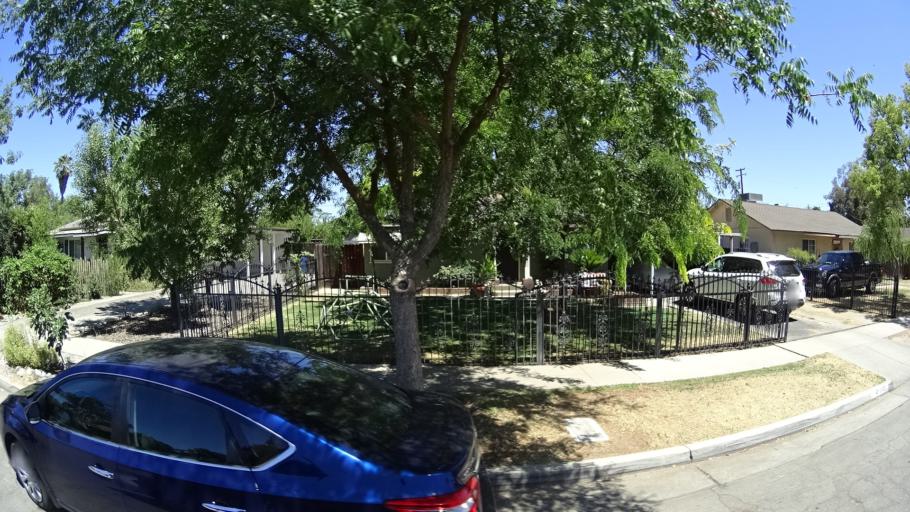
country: US
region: California
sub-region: Fresno County
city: Fresno
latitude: 36.7775
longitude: -119.8231
